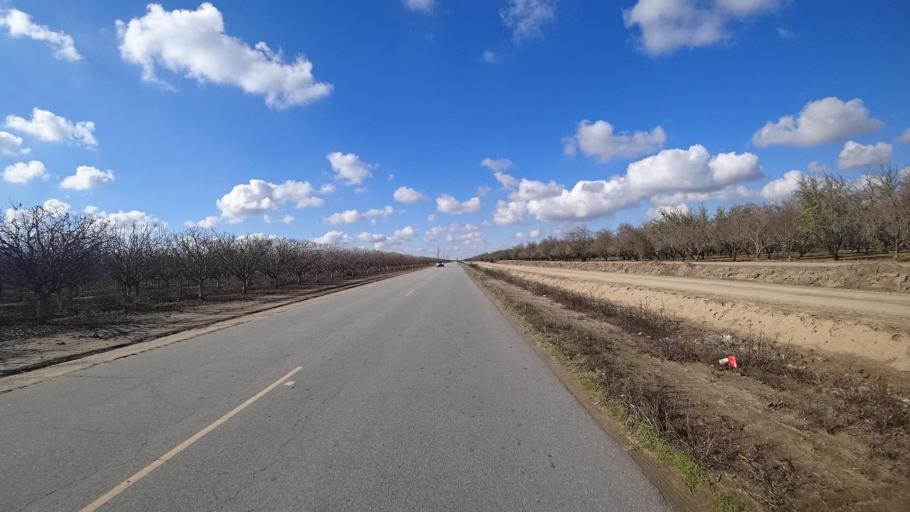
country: US
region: California
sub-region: Kern County
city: Wasco
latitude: 35.6742
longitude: -119.3142
